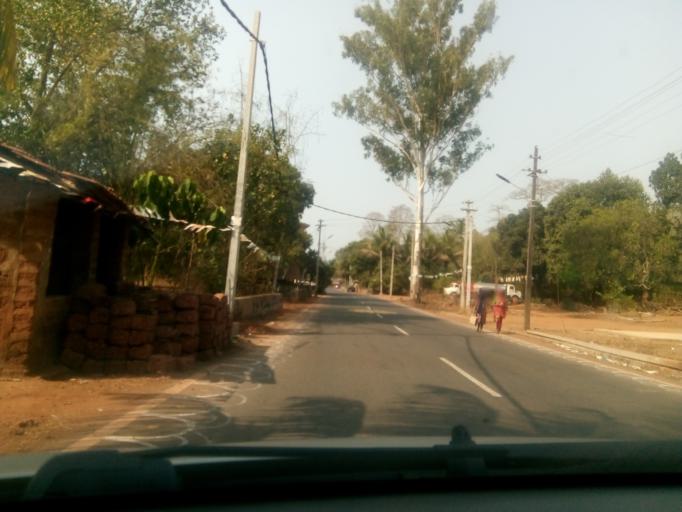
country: IN
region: Goa
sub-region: North Goa
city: Pernem
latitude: 15.7069
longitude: 73.8530
